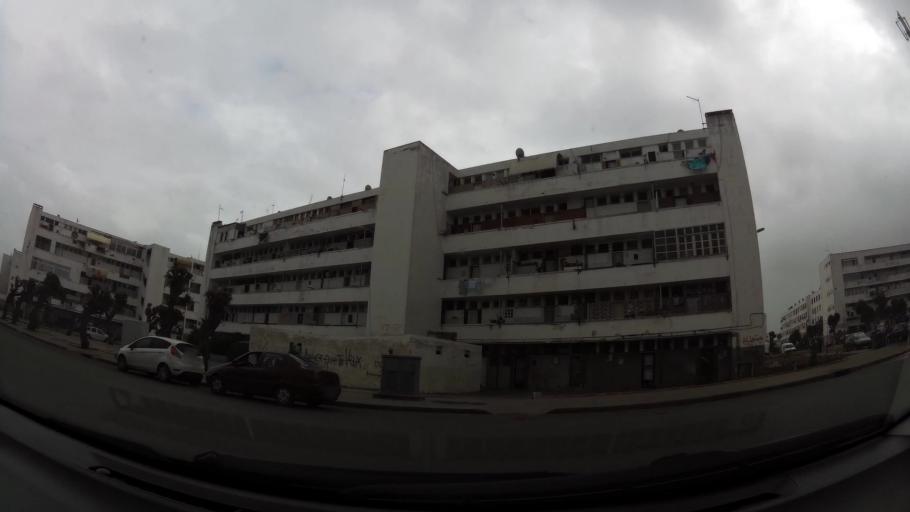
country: MA
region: Grand Casablanca
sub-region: Casablanca
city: Casablanca
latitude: 33.6038
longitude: -7.6524
